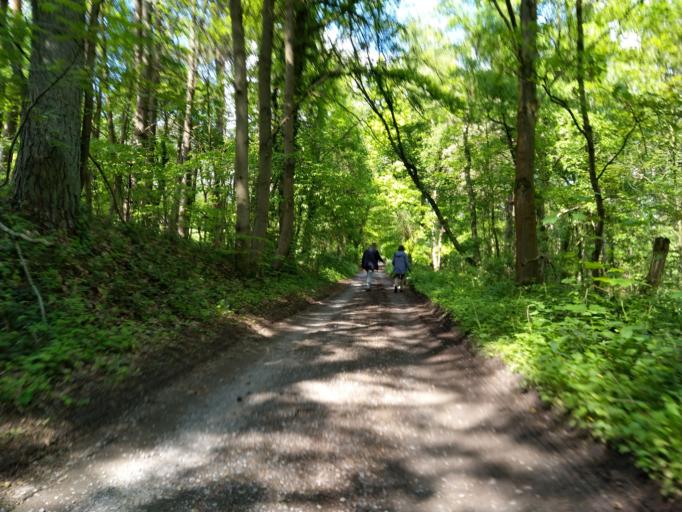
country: BE
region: Wallonia
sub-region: Province du Hainaut
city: Jurbise
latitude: 50.4993
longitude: 3.9248
